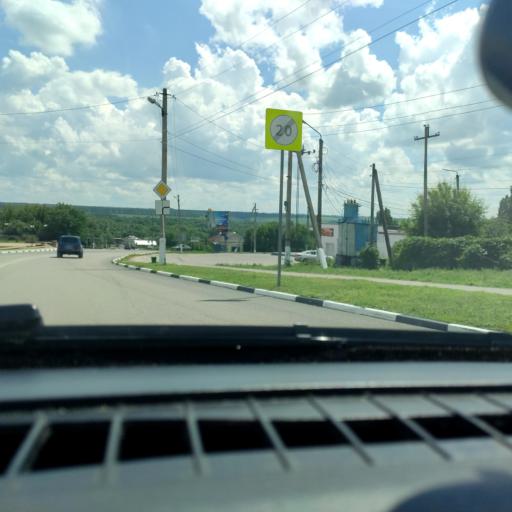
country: RU
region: Voronezj
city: Strelitsa
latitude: 51.5750
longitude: 38.7891
